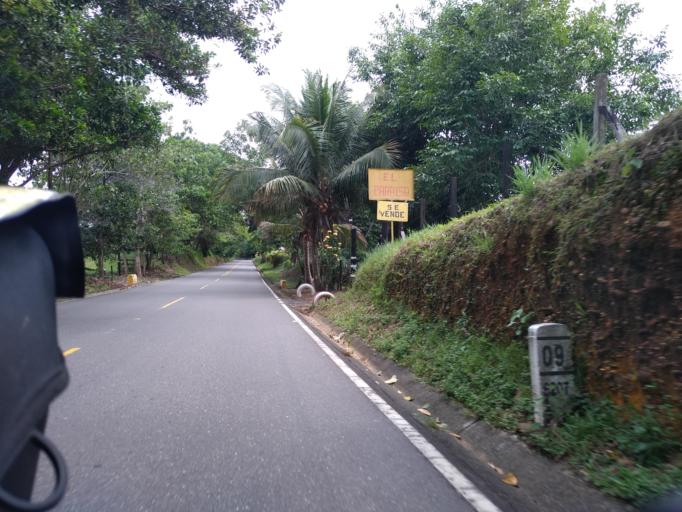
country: CO
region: Santander
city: Cimitarra
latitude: 6.4662
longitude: -74.0292
